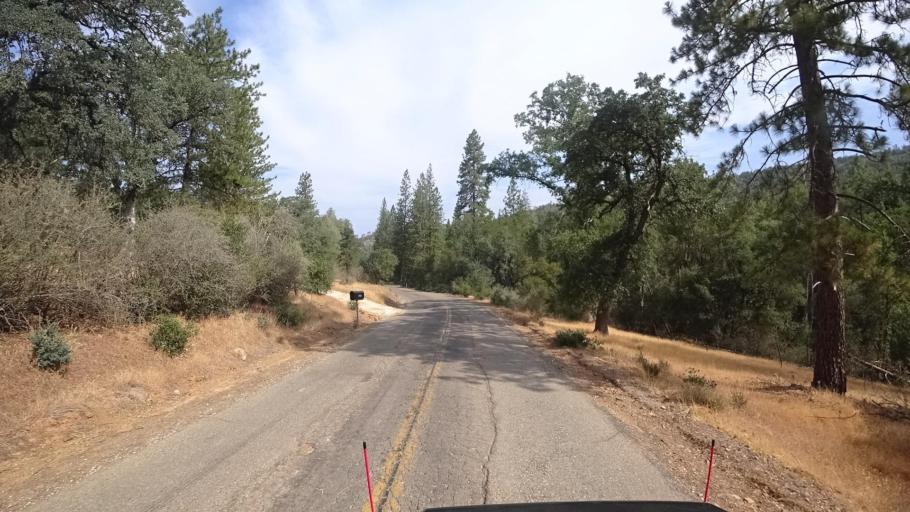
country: US
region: California
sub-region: Mariposa County
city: Mariposa
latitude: 37.5454
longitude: -119.9942
